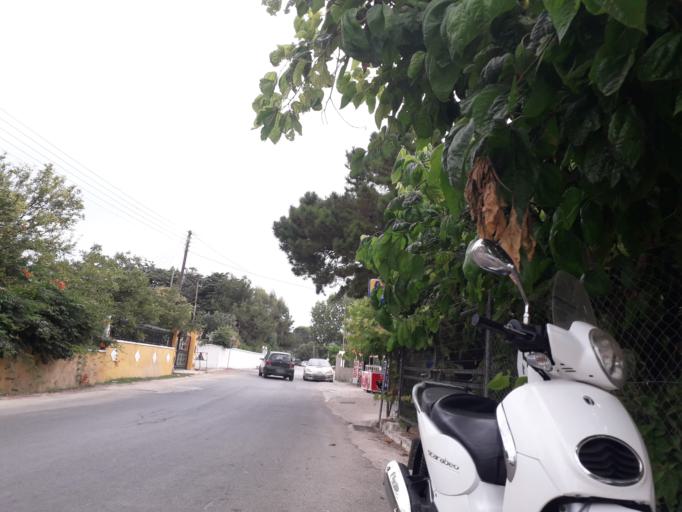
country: GR
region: Ionian Islands
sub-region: Nomos Kerkyras
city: Perivoli
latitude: 39.4291
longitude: 19.9499
